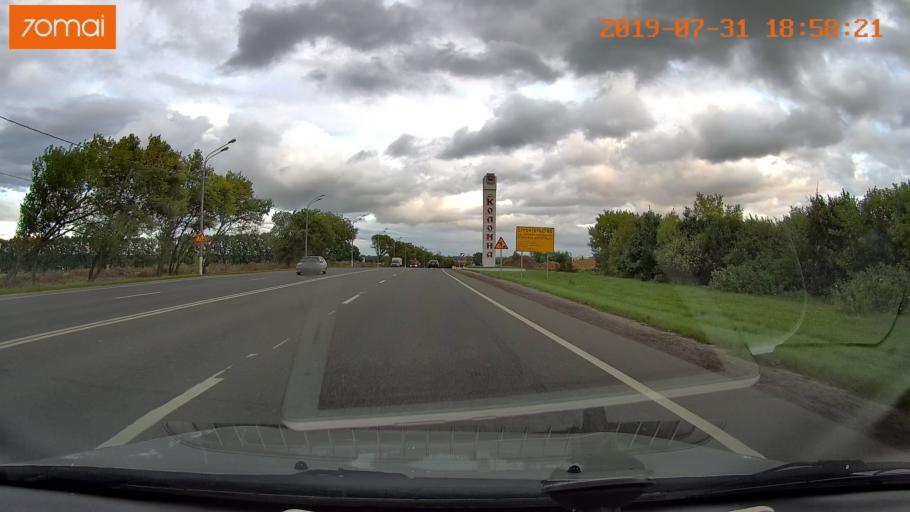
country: RU
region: Moskovskaya
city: Raduzhnyy
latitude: 55.1474
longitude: 38.7036
